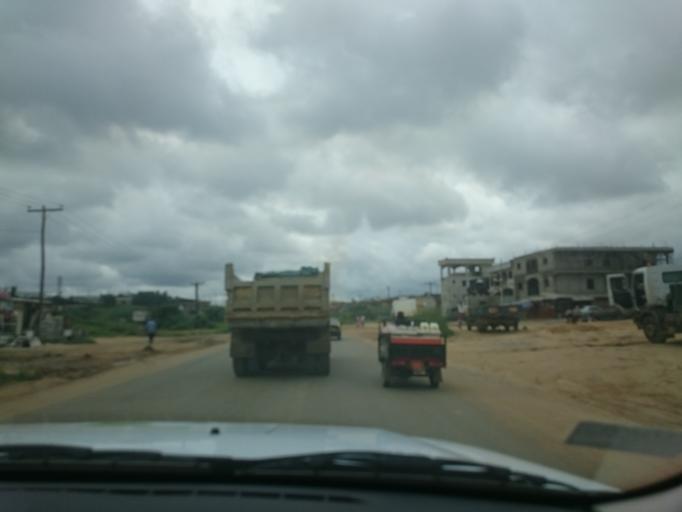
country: CM
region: Littoral
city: Douala
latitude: 3.9933
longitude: 9.7882
